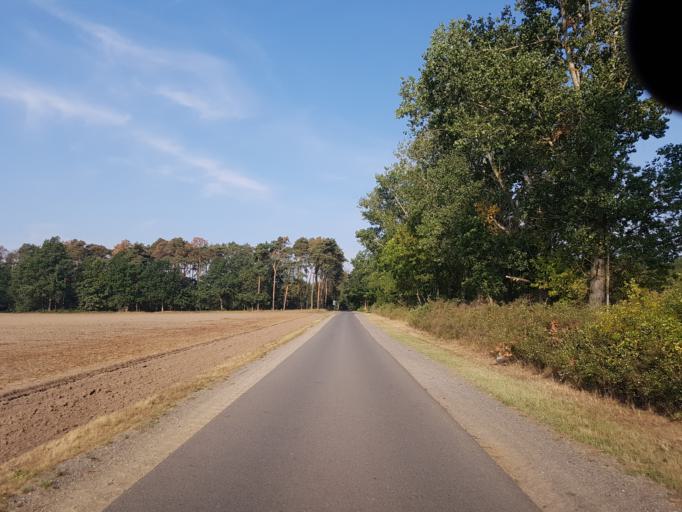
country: DE
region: Brandenburg
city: Sonnewalde
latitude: 51.6870
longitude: 13.6995
